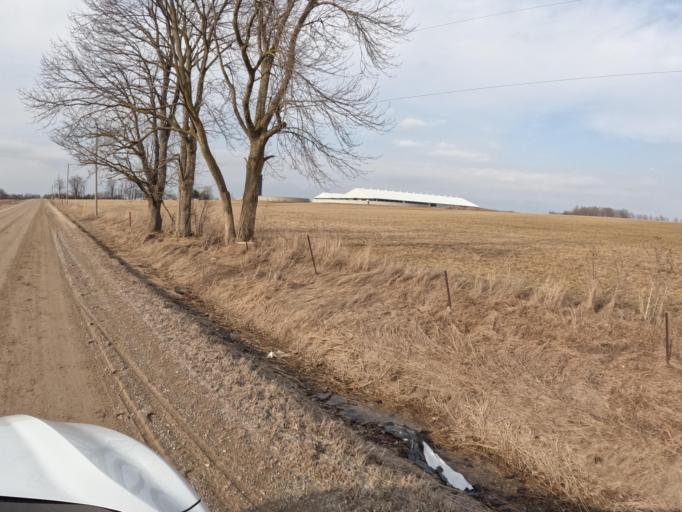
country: CA
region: Ontario
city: Orangeville
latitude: 43.9006
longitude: -80.2679
